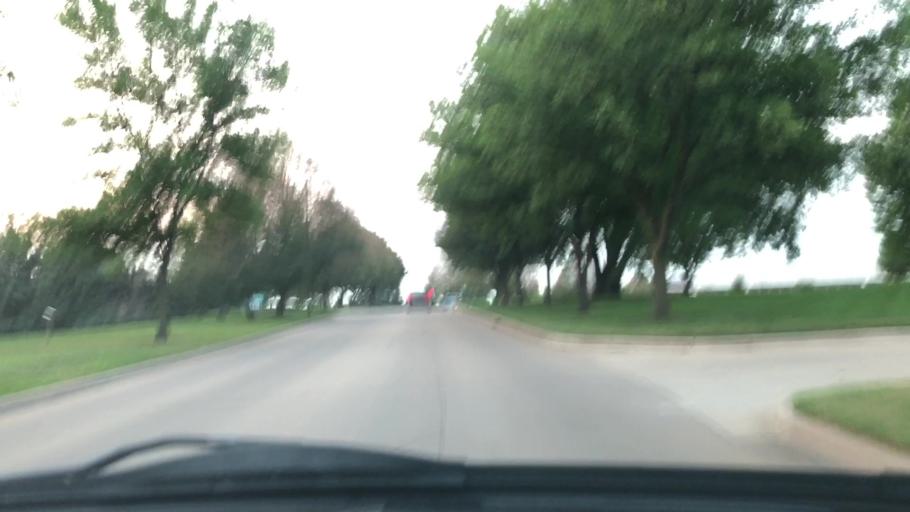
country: US
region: Iowa
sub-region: Johnson County
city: North Liberty
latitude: 41.7124
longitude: -91.6051
